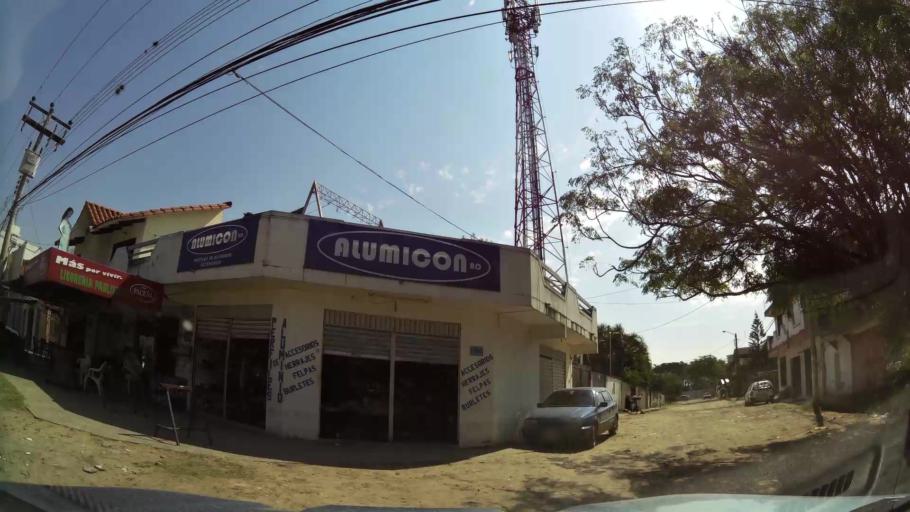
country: BO
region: Santa Cruz
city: Santa Cruz de la Sierra
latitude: -17.7512
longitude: -63.1652
